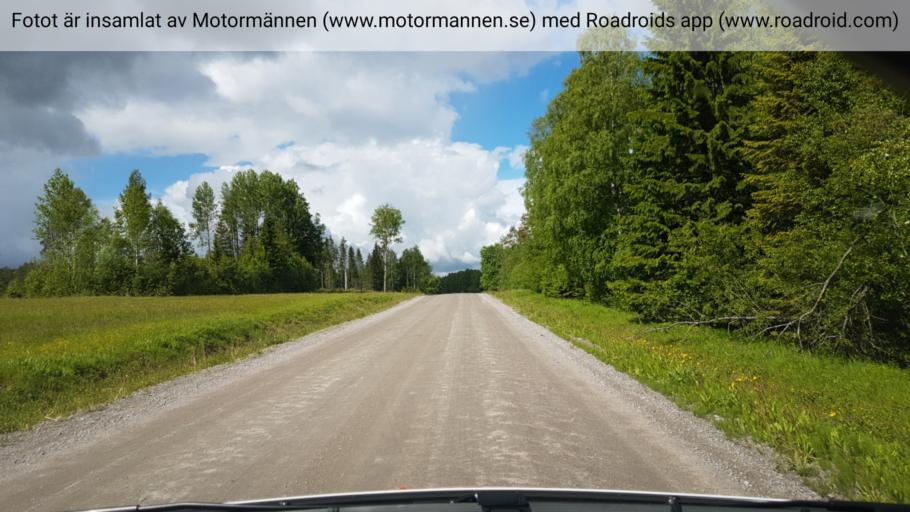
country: SE
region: Vaesterbotten
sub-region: Vannas Kommun
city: Vannasby
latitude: 63.8310
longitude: 19.9846
